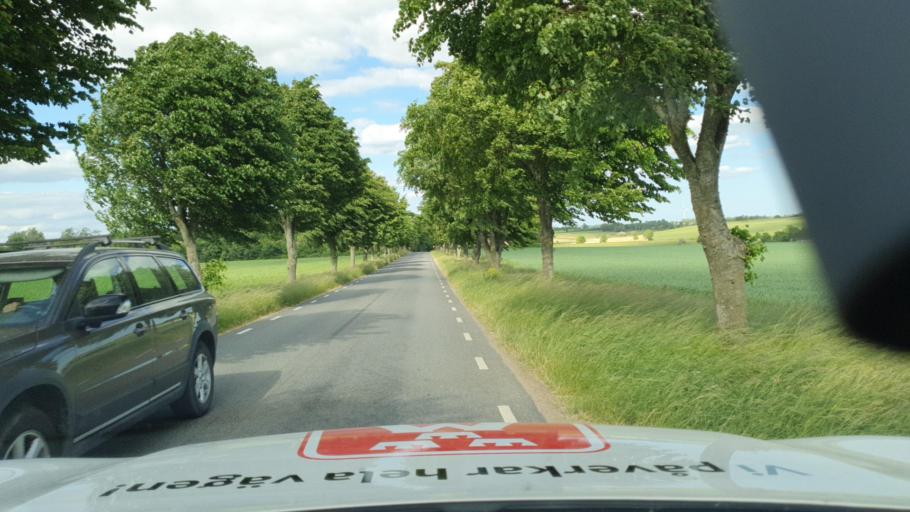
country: SE
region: Skane
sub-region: Tomelilla Kommun
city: Tomelilla
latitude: 55.4873
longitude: 14.0405
